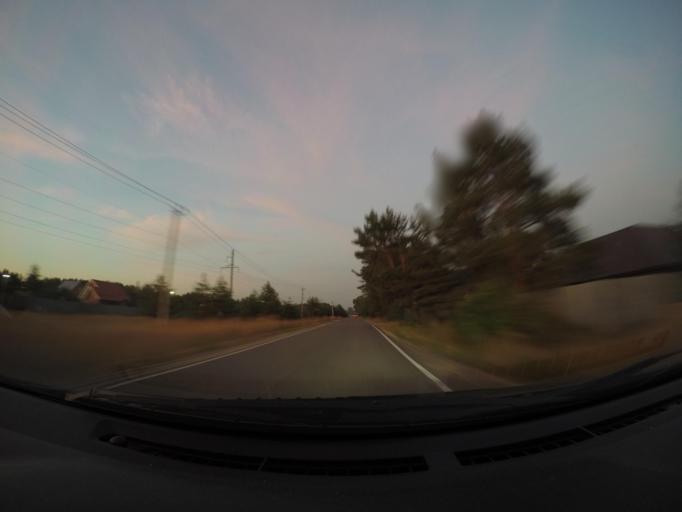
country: RU
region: Moskovskaya
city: Rechitsy
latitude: 55.5422
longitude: 38.4324
